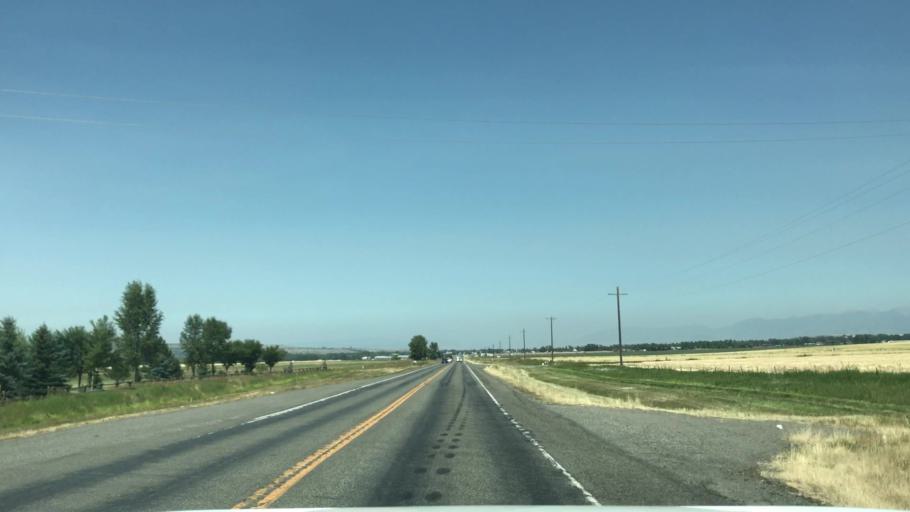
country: US
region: Montana
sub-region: Gallatin County
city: Four Corners
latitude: 45.5656
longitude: -111.1968
